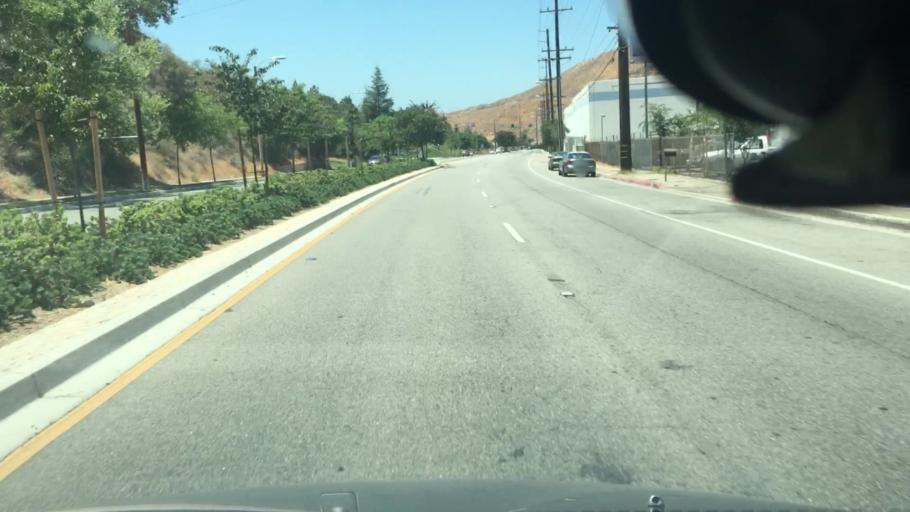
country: US
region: California
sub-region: Los Angeles County
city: Santa Clarita
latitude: 34.4343
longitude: -118.4361
